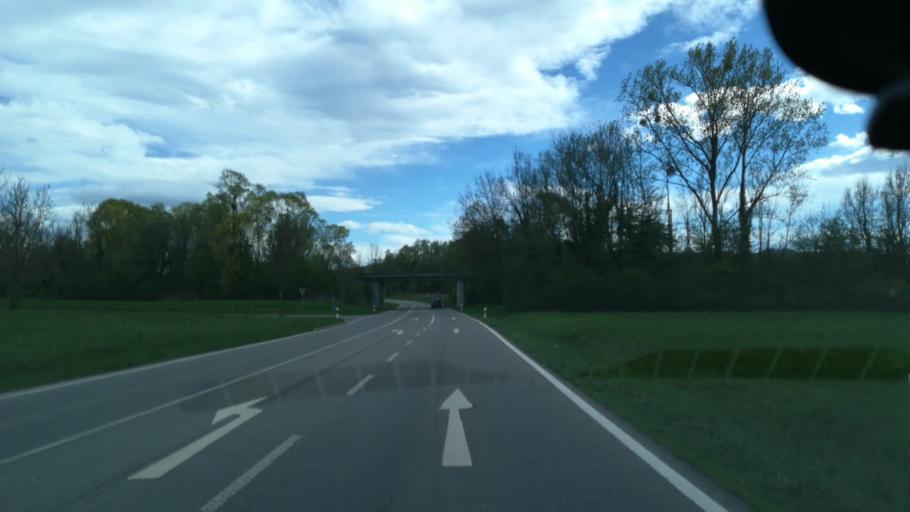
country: DE
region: Baden-Wuerttemberg
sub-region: Freiburg Region
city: Moos
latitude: 47.7508
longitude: 8.9228
